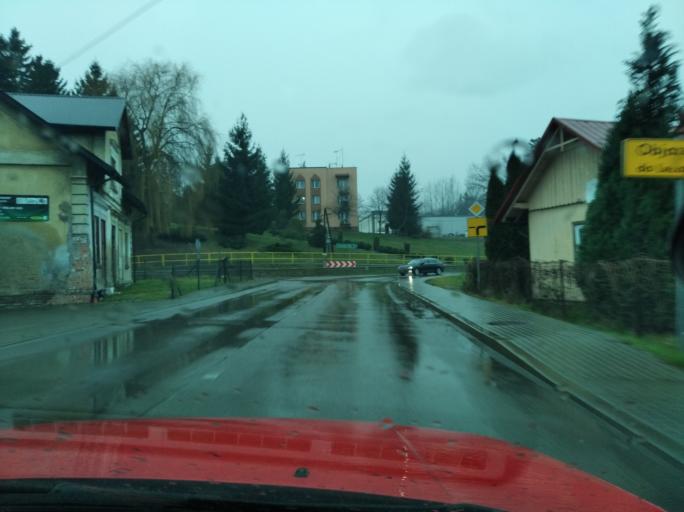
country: PL
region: Subcarpathian Voivodeship
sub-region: Powiat lancucki
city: Krzemienica
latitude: 50.0726
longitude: 22.1903
